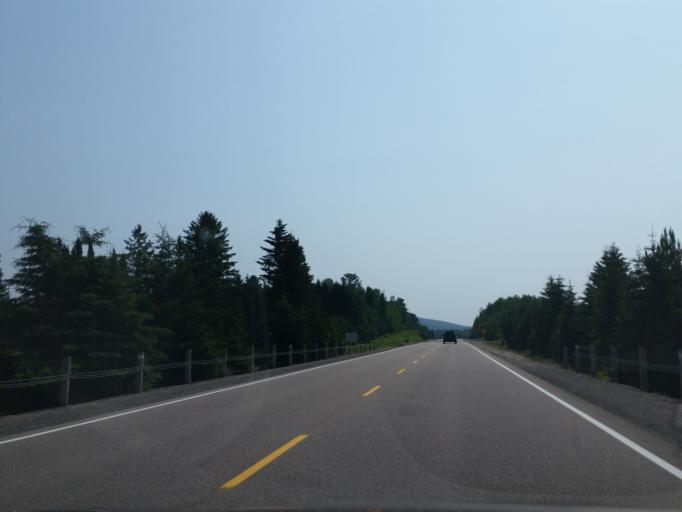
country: CA
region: Ontario
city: Mattawa
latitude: 46.3049
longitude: -78.5858
